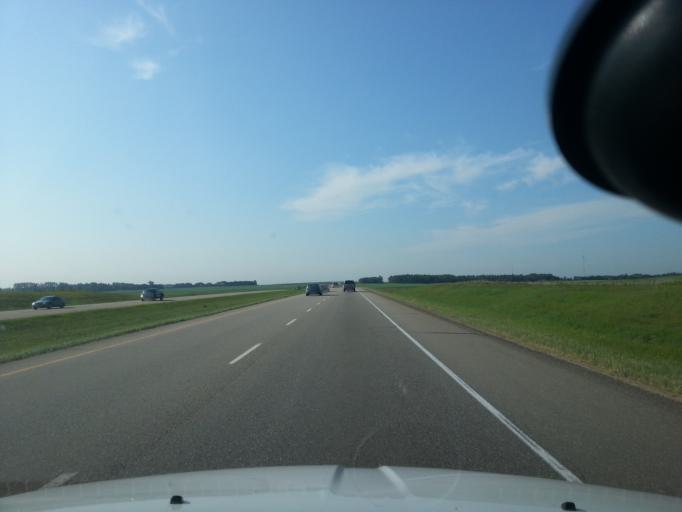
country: CA
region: Alberta
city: Ponoka
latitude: 52.7553
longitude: -113.6441
